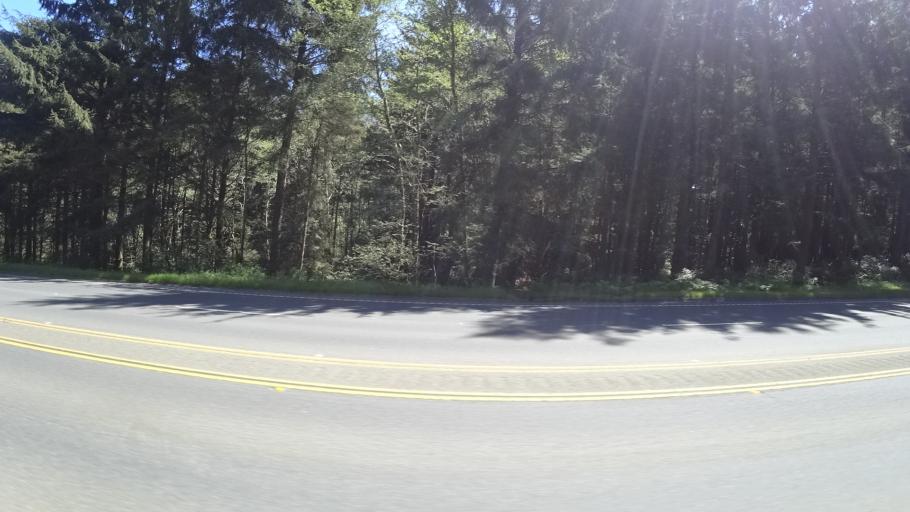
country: US
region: California
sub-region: Humboldt County
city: Westhaven-Moonstone
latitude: 41.1489
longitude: -124.1359
